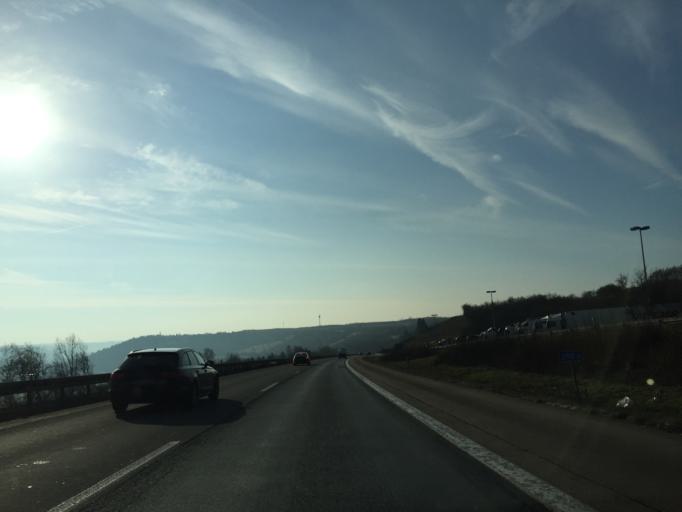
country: DE
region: Bavaria
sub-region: Regierungsbezirk Unterfranken
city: Randersacker
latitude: 49.7509
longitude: 9.9643
